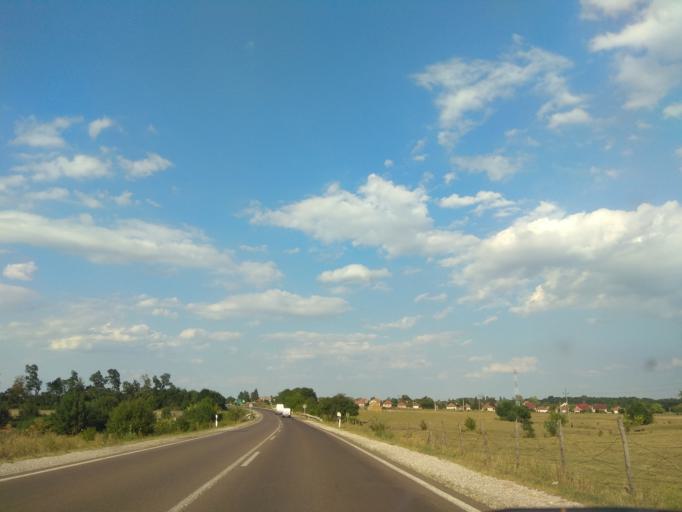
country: HU
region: Borsod-Abauj-Zemplen
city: Mezokeresztes
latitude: 47.8494
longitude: 20.6647
